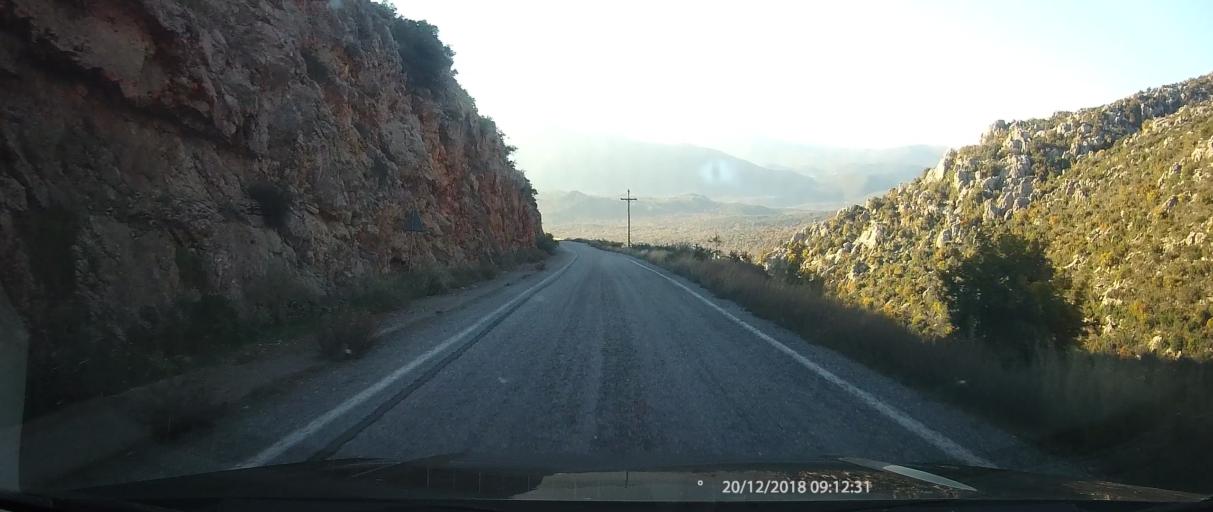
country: GR
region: Peloponnese
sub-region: Nomos Lakonias
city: Sykea
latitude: 36.9061
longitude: 22.9964
